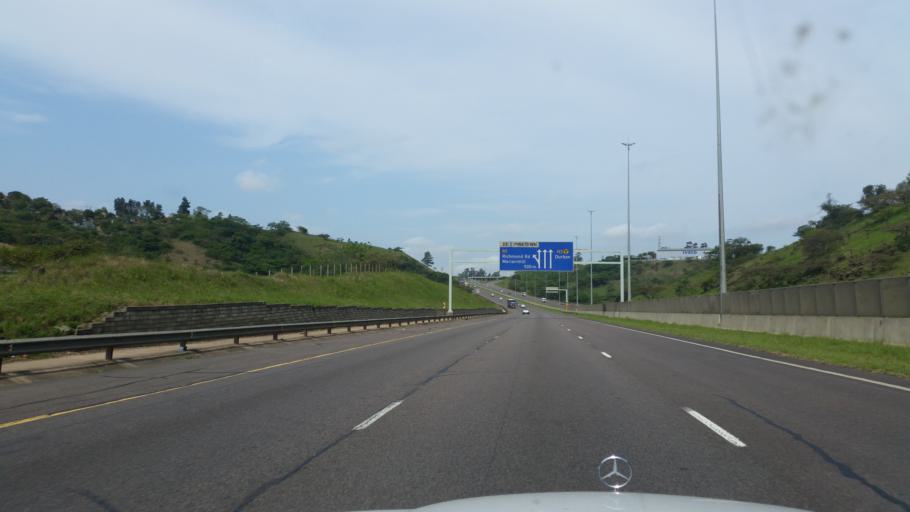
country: ZA
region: KwaZulu-Natal
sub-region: eThekwini Metropolitan Municipality
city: Berea
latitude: -29.8269
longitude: 30.8206
